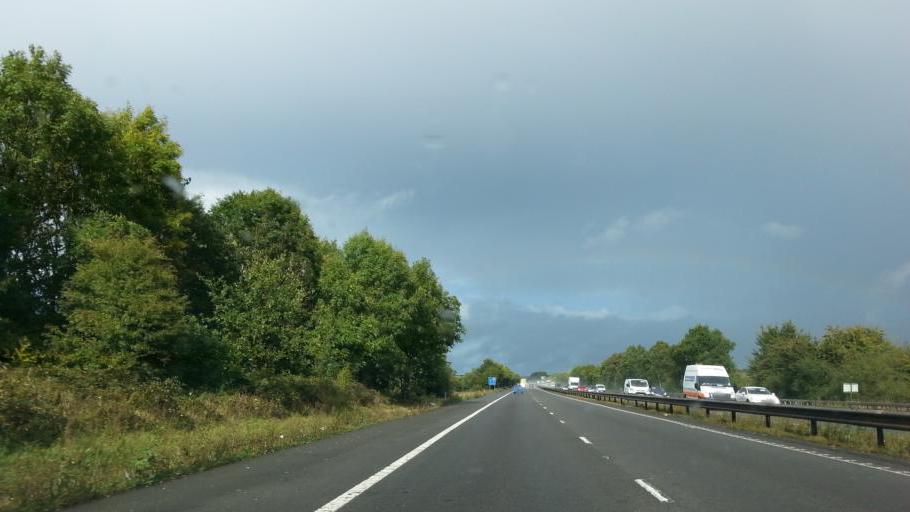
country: GB
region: England
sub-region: Derbyshire
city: Netherseal
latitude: 52.6615
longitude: -1.5767
